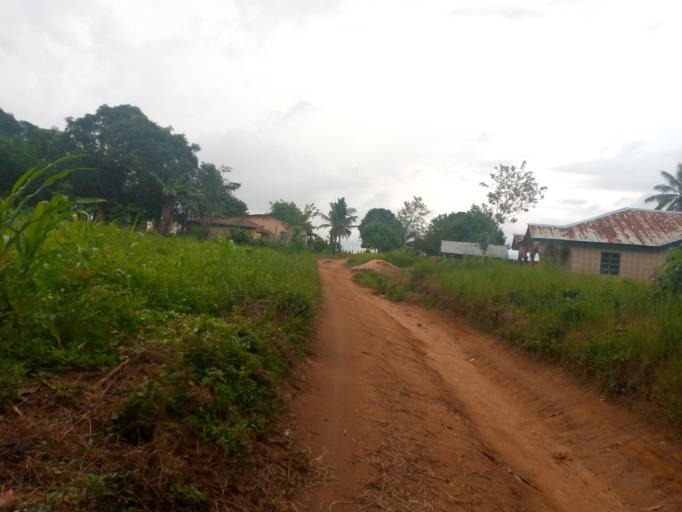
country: SL
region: Southern Province
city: Sumbuya
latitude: 7.6023
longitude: -12.1635
